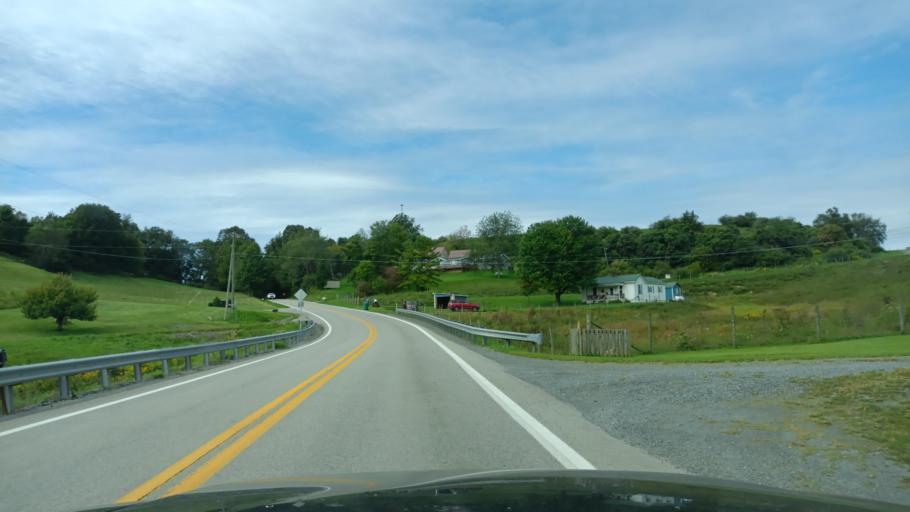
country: US
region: West Virginia
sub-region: Harrison County
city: Bridgeport
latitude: 39.3035
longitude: -80.1598
